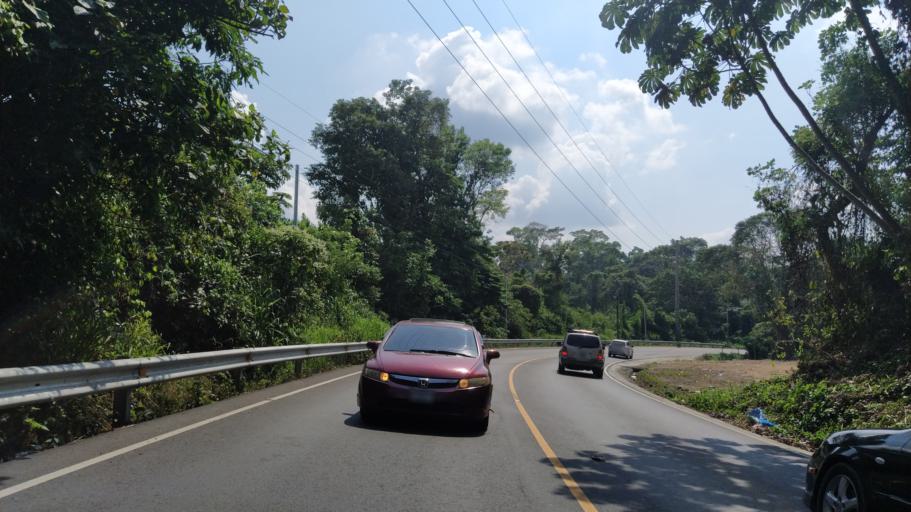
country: GT
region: Retalhuleu
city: San Felipe
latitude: 14.6255
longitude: -91.5847
